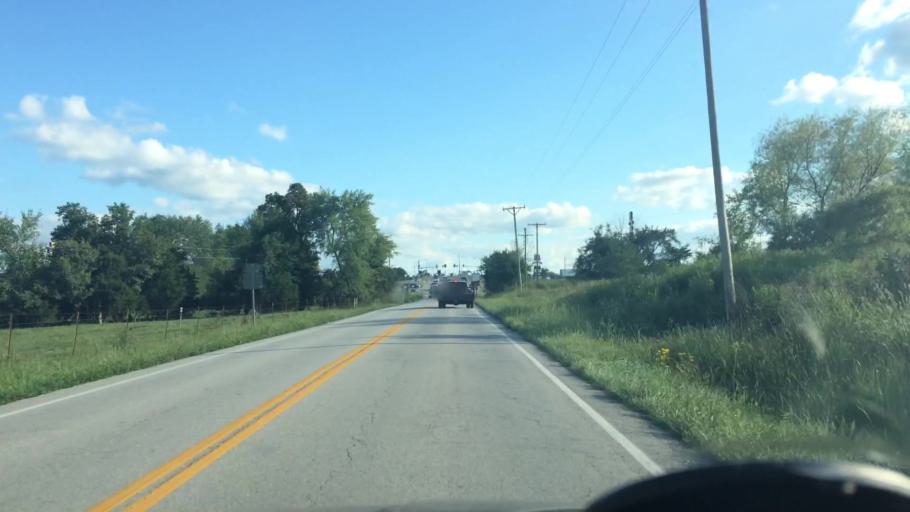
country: US
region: Missouri
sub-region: Greene County
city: Strafford
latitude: 37.2789
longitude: -93.1133
